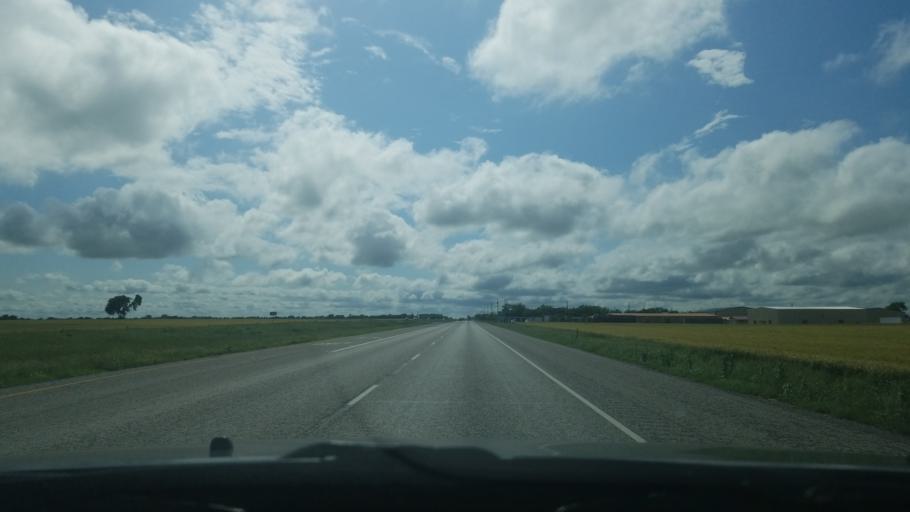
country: US
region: Texas
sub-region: Denton County
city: Ponder
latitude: 33.2377
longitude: -97.3010
